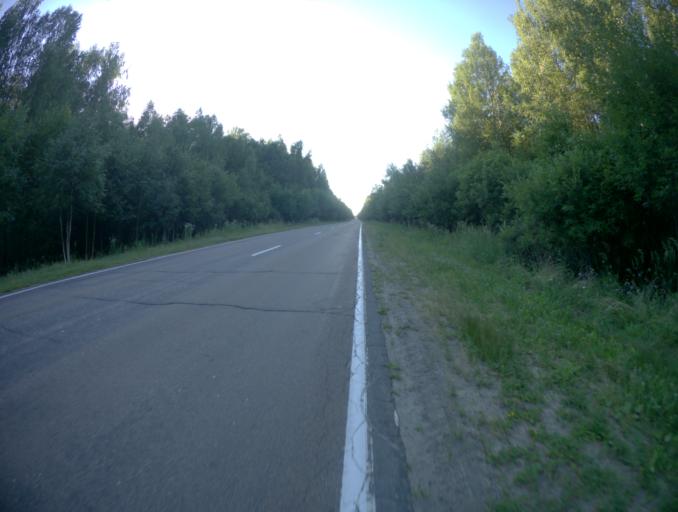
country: RU
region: Vladimir
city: Galitsy
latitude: 56.1386
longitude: 42.8711
